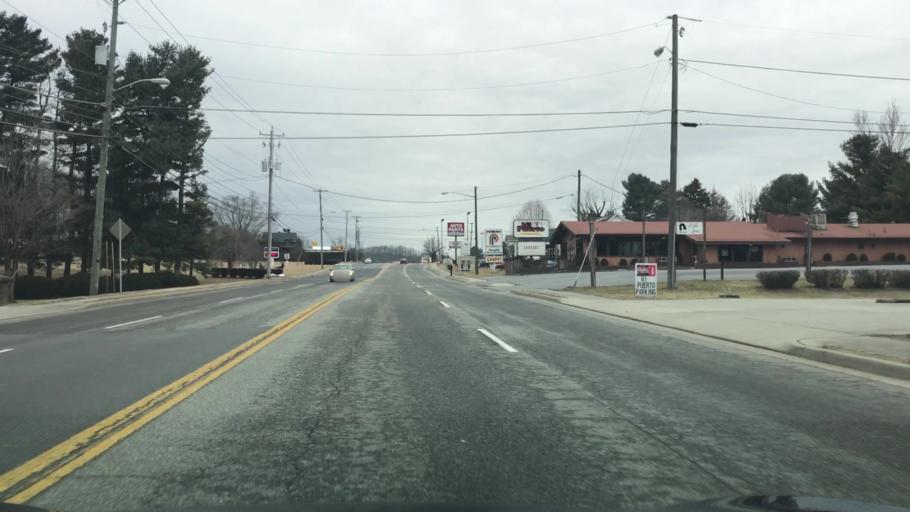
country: US
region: Virginia
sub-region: Smyth County
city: Marion
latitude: 36.8455
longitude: -81.4963
